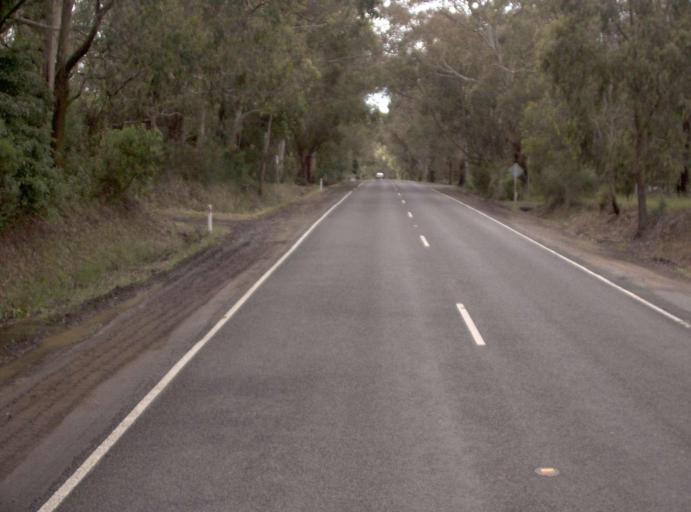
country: AU
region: Victoria
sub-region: Mornington Peninsula
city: Dromana
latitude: -38.3661
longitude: 144.9964
